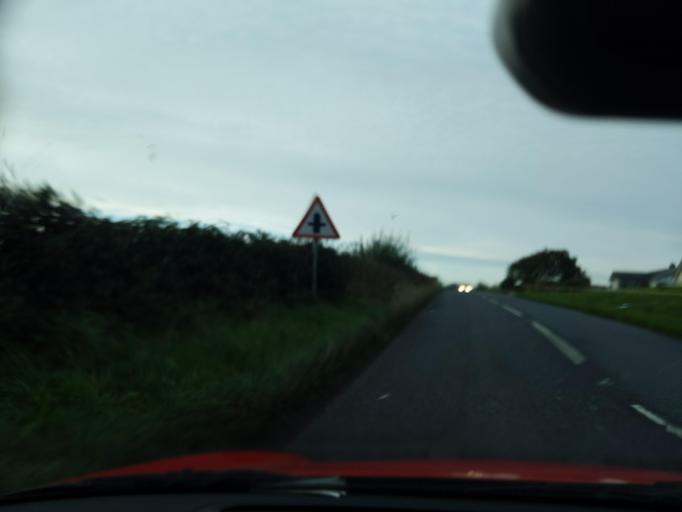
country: GB
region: England
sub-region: Devon
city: Great Torrington
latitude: 50.9312
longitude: -4.1514
